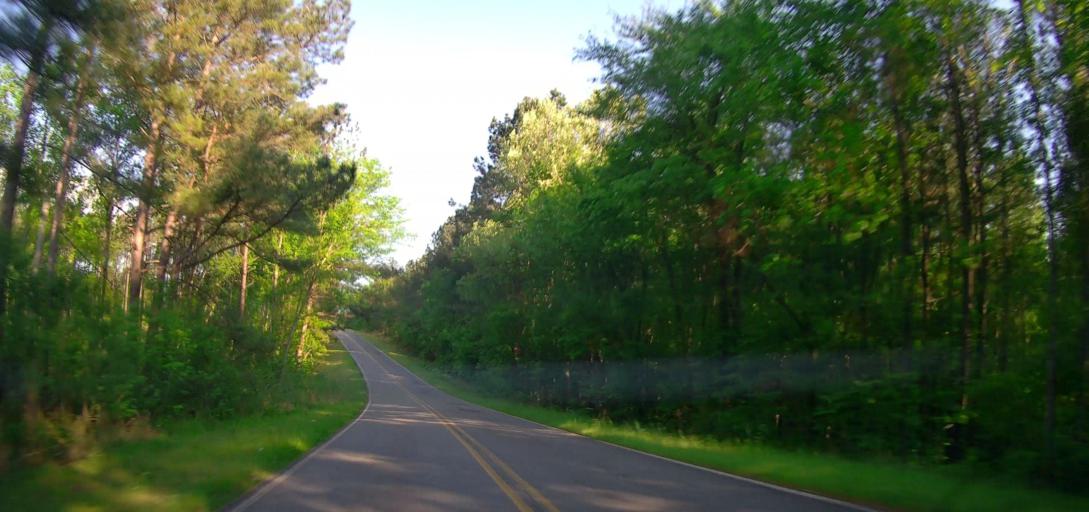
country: US
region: Georgia
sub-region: Putnam County
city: Eatonton
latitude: 33.2744
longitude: -83.3086
